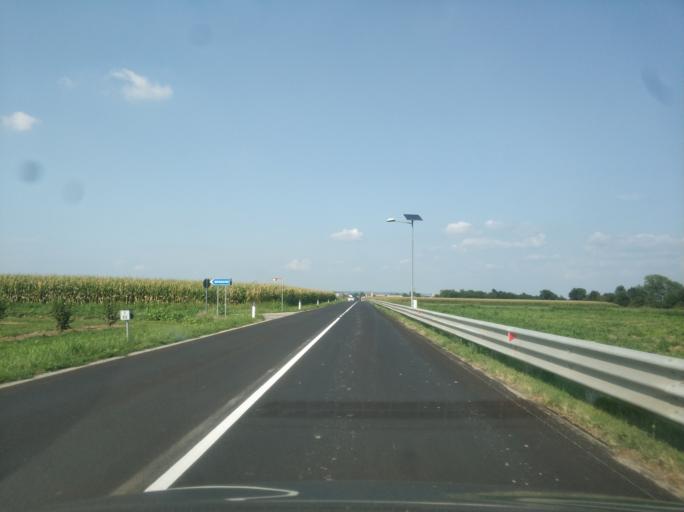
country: IT
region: Piedmont
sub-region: Provincia di Cuneo
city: Cervere
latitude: 44.6186
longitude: 7.7779
